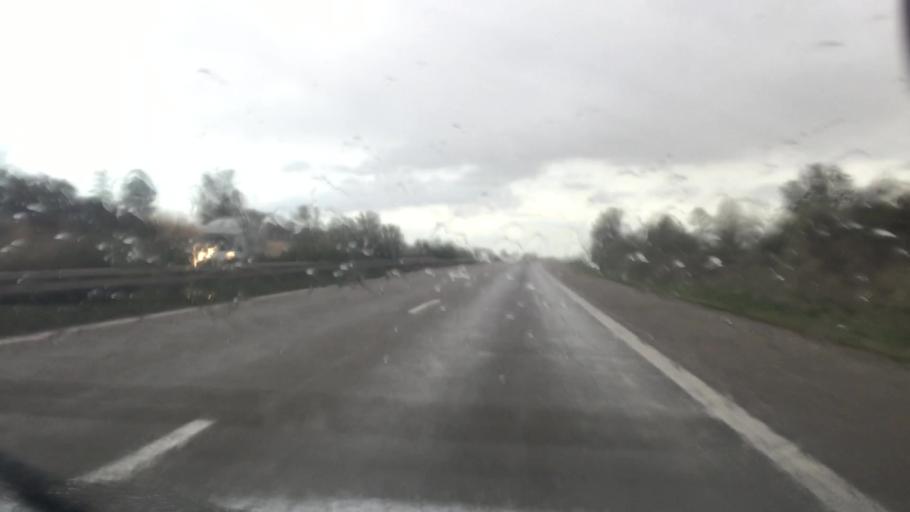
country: DE
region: Saxony-Anhalt
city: Eickendorf
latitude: 51.9372
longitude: 11.6955
